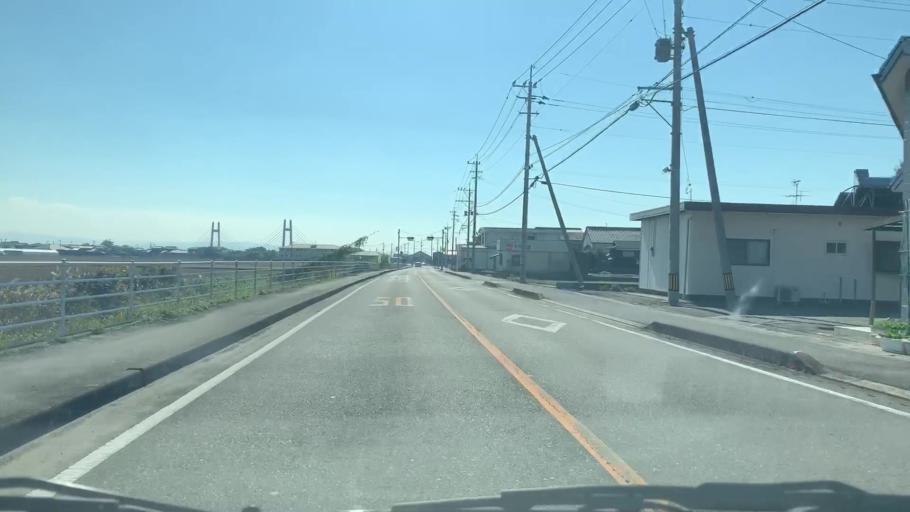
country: JP
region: Saga Prefecture
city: Kanzakimachi-kanzaki
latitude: 33.2936
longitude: 130.4451
